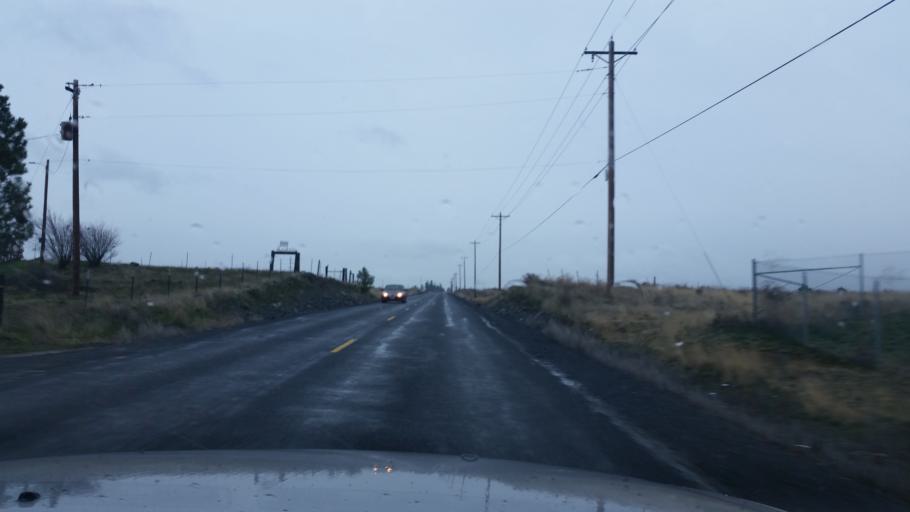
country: US
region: Washington
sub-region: Spokane County
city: Airway Heights
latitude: 47.6718
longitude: -117.5702
